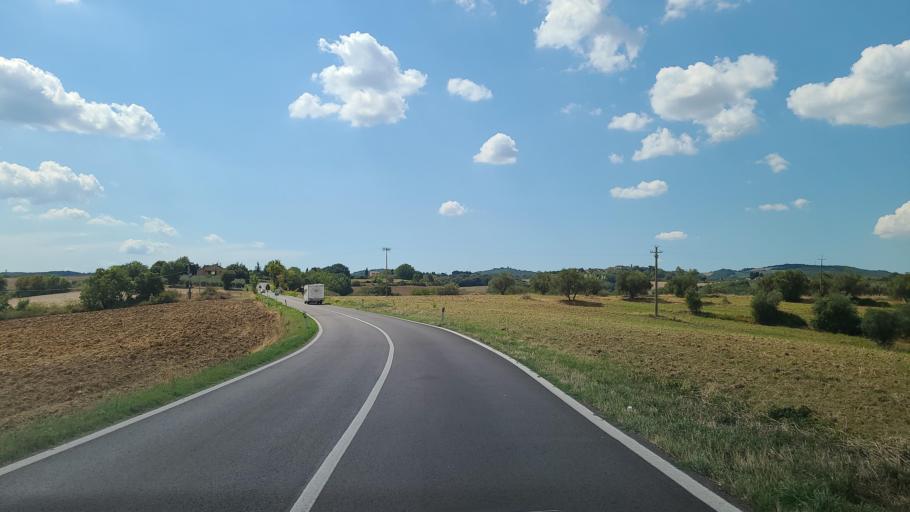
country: IT
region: Tuscany
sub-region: Provincia di Siena
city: Casole d'Elsa
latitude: 43.4047
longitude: 11.0410
